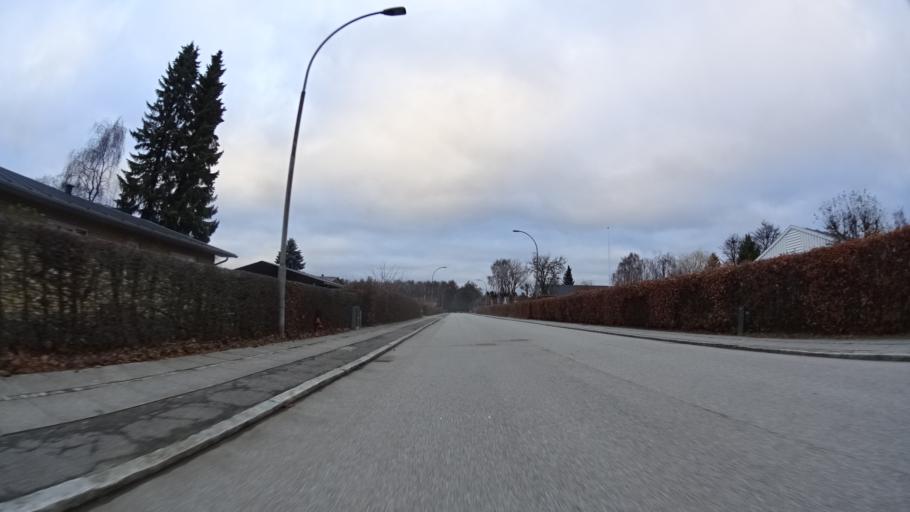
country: DK
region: Central Jutland
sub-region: Arhus Kommune
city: Stavtrup
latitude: 56.1594
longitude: 10.1067
